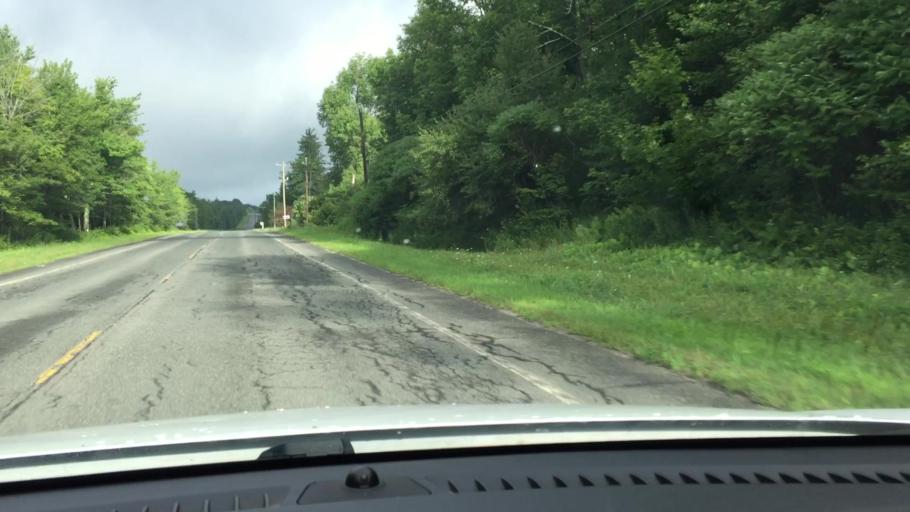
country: US
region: Massachusetts
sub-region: Berkshire County
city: Hinsdale
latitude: 42.4355
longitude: -73.0336
